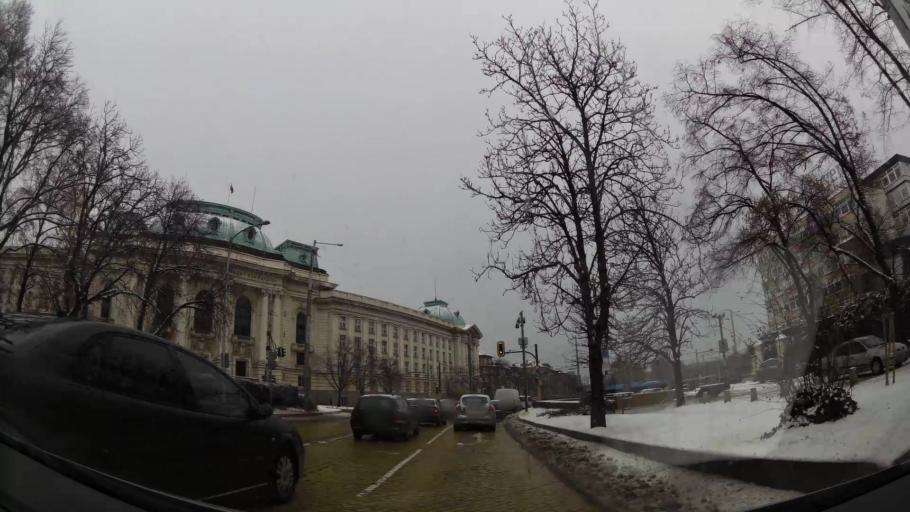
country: BG
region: Sofia-Capital
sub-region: Stolichna Obshtina
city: Sofia
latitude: 42.6934
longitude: 23.3337
